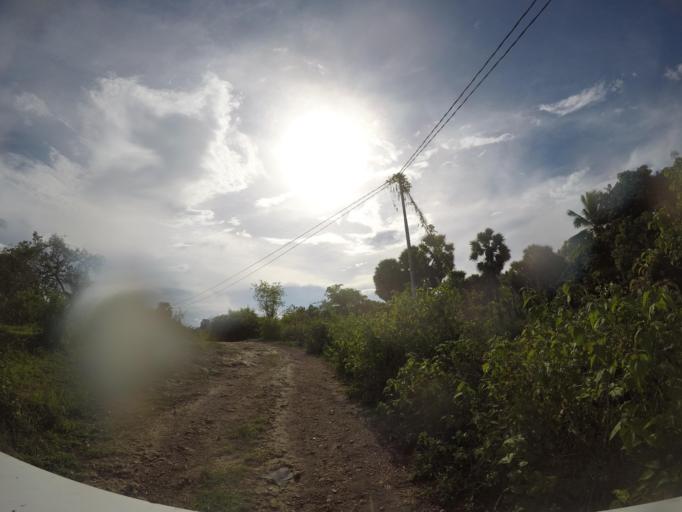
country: TL
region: Baucau
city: Baucau
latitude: -8.5049
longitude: 126.4484
